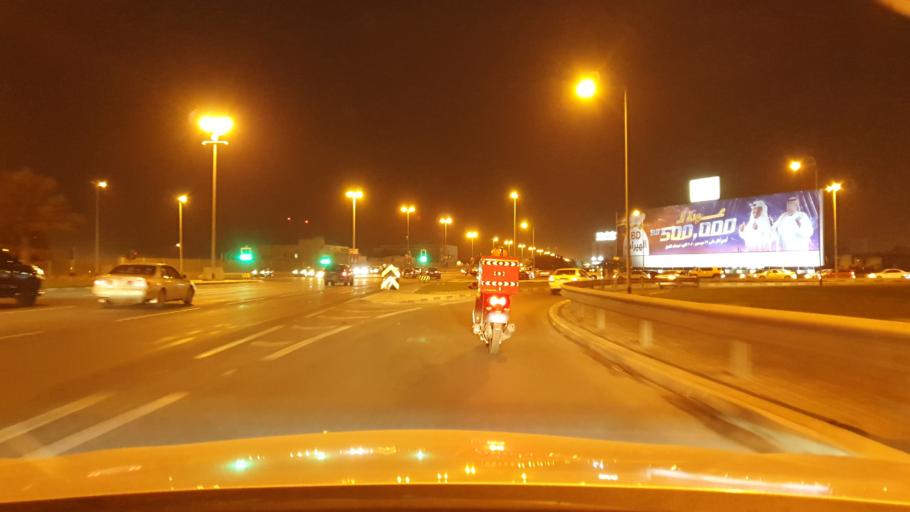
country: BH
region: Muharraq
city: Al Hadd
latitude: 26.2620
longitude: 50.6401
